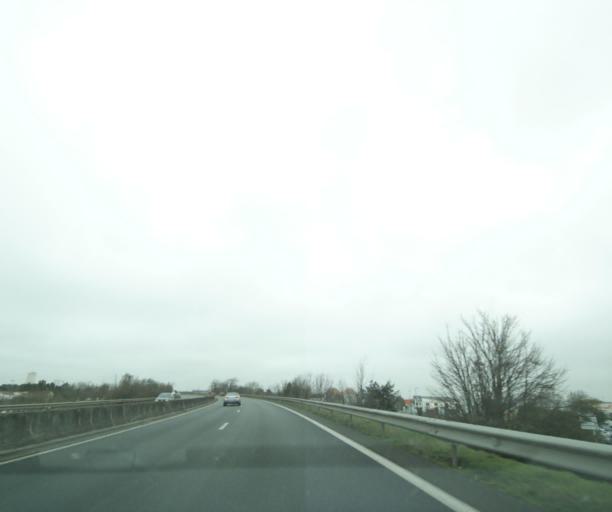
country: FR
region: Poitou-Charentes
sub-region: Departement de la Charente-Maritime
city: Aytre
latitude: 46.1303
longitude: -1.1016
